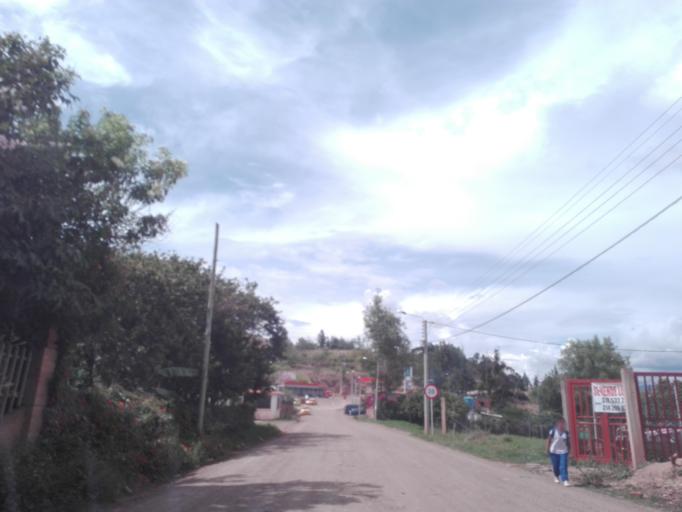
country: CO
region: Boyaca
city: Raquira
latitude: 5.5723
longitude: -73.6507
